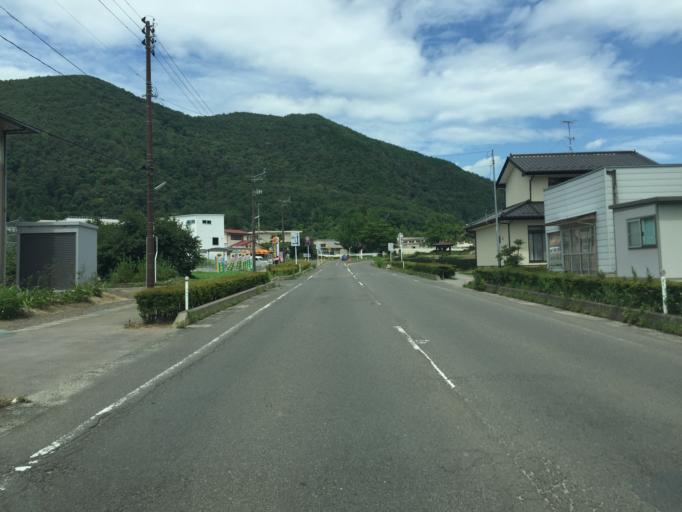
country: JP
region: Fukushima
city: Fukushima-shi
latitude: 37.8121
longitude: 140.4156
